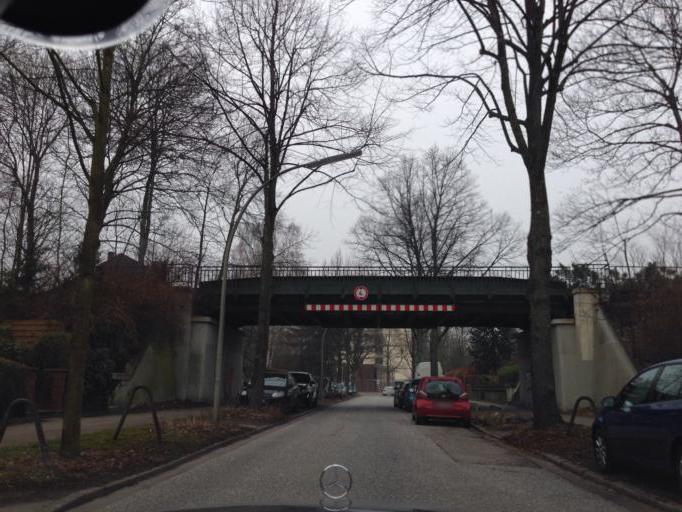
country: DE
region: Hamburg
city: Marienthal
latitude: 53.5933
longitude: 10.0813
